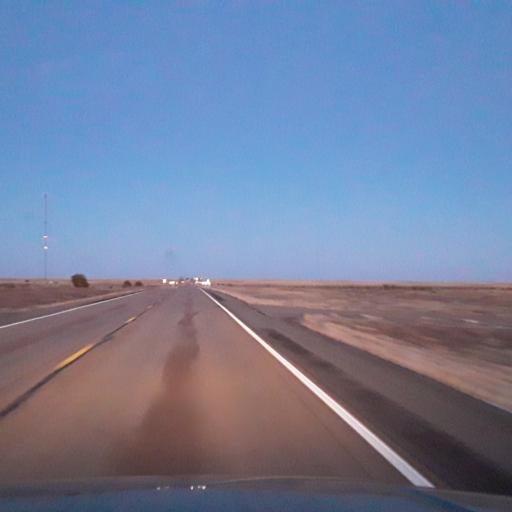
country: US
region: New Mexico
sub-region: Guadalupe County
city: Santa Rosa
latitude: 34.7817
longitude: -104.9404
